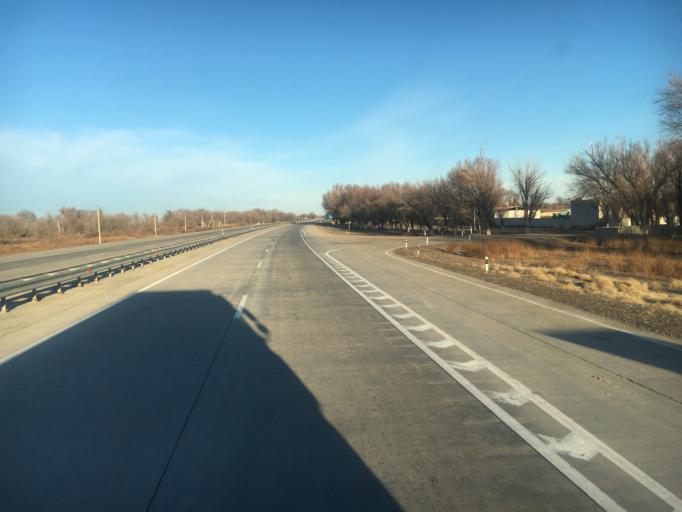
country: KZ
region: Ongtustik Qazaqstan
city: Turkestan
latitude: 43.1449
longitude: 68.5780
